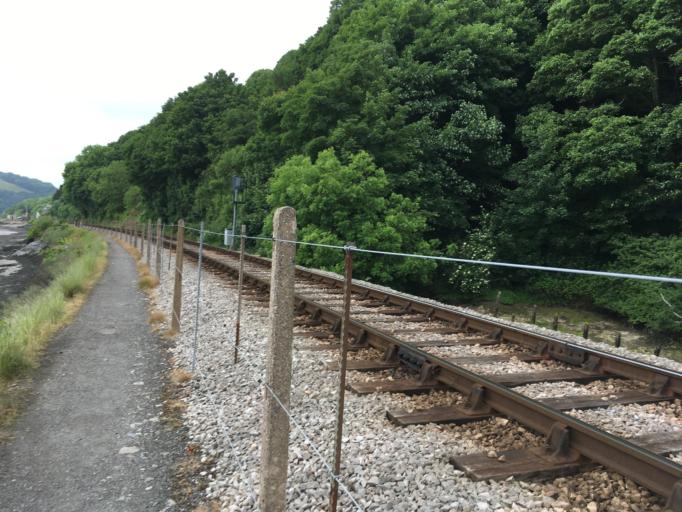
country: GB
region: England
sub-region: Devon
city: Dartmouth
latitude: 50.3570
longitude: -3.5705
